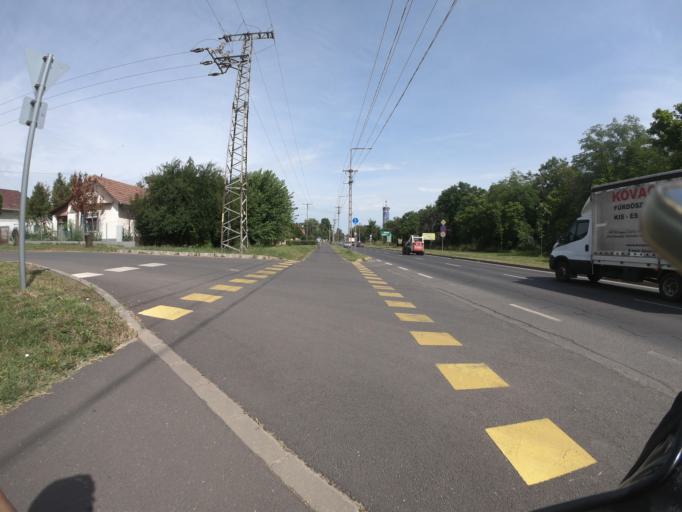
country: HU
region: Jasz-Nagykun-Szolnok
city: Tiszafured
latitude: 47.6162
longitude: 20.7485
